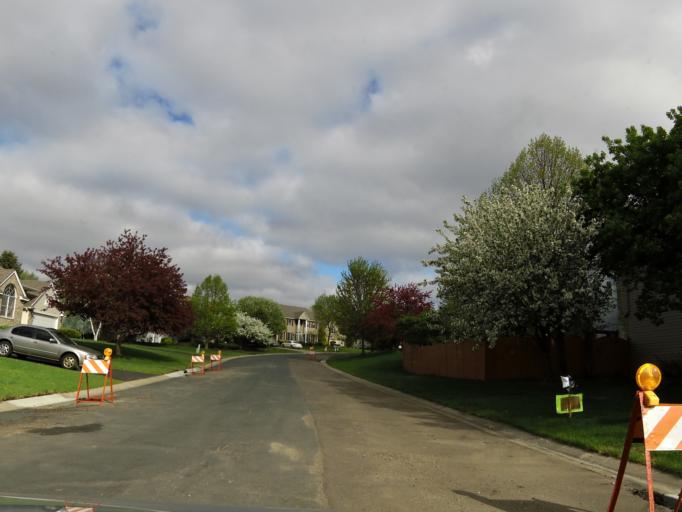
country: US
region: Minnesota
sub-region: Washington County
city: Woodbury
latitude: 44.9235
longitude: -92.9206
